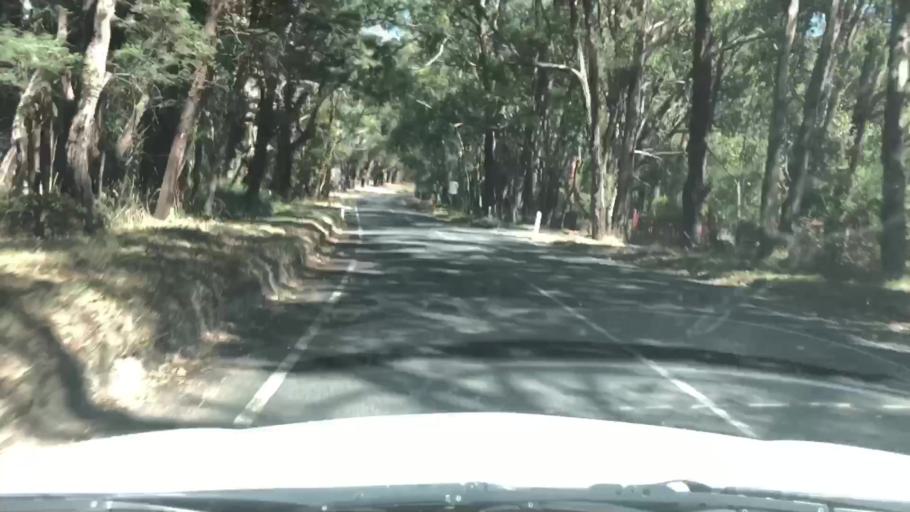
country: AU
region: Victoria
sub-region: Yarra Ranges
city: Macclesfield
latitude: -37.8340
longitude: 145.4872
